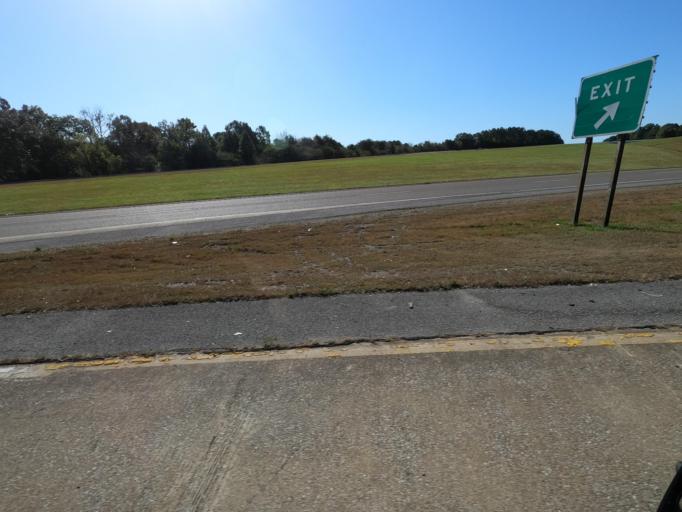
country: US
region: Tennessee
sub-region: Hamilton County
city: Soddy-Daisy
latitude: 35.3036
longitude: -85.1491
